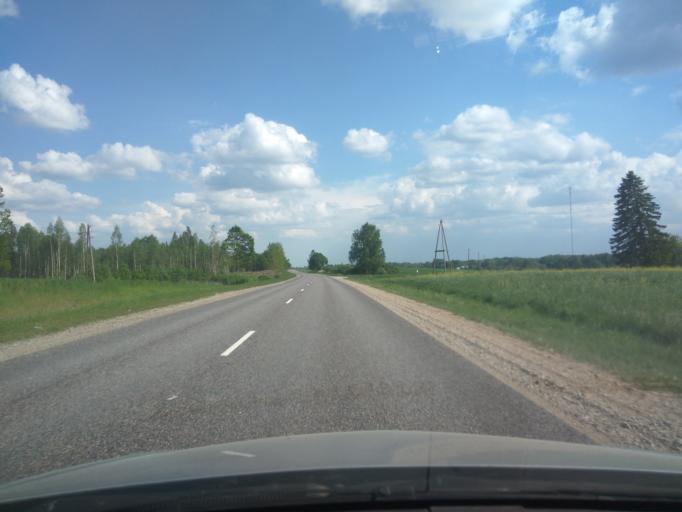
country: LV
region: Kuldigas Rajons
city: Kuldiga
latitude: 57.0320
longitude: 21.8443
